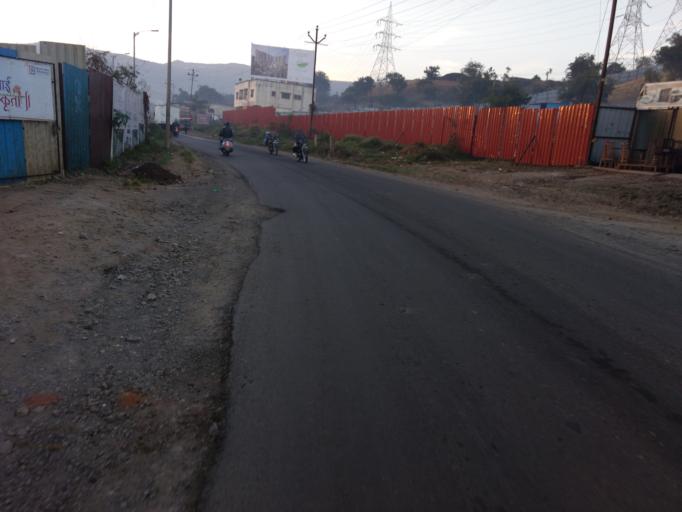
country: IN
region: Maharashtra
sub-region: Pune Division
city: Pune
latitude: 18.4324
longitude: 73.8976
